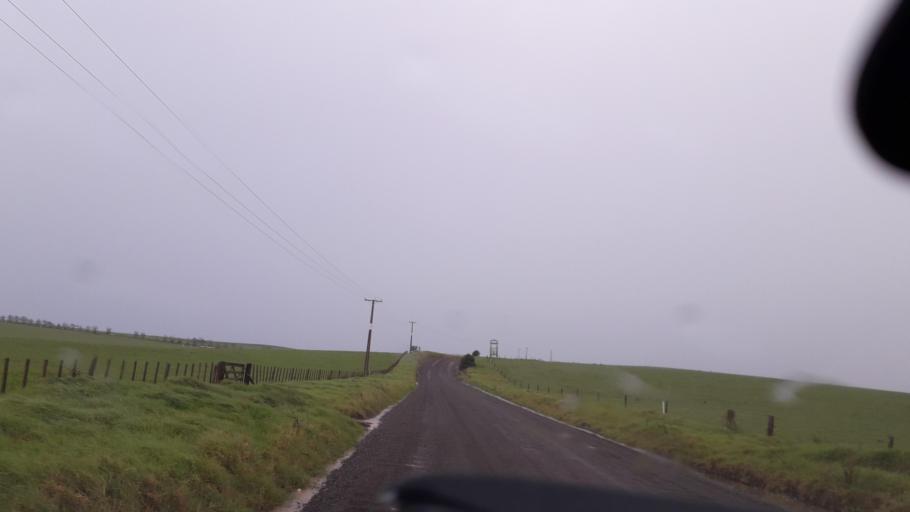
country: NZ
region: Northland
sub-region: Far North District
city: Kerikeri
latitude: -35.1315
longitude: 174.0028
